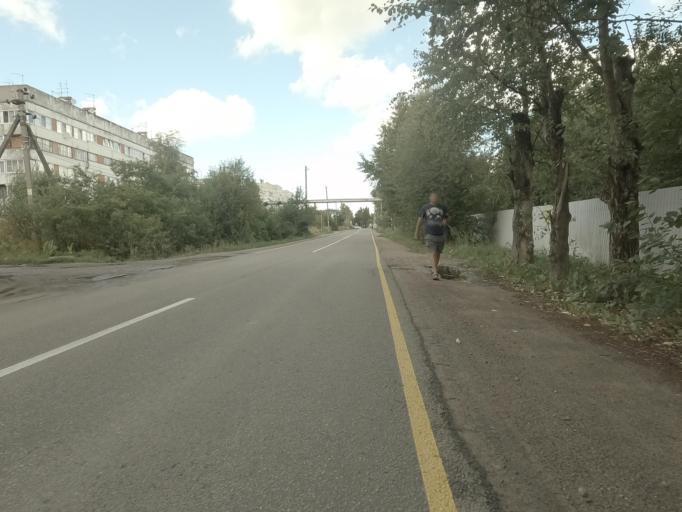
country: RU
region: Leningrad
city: Shcheglovo
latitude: 60.0264
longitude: 30.7529
